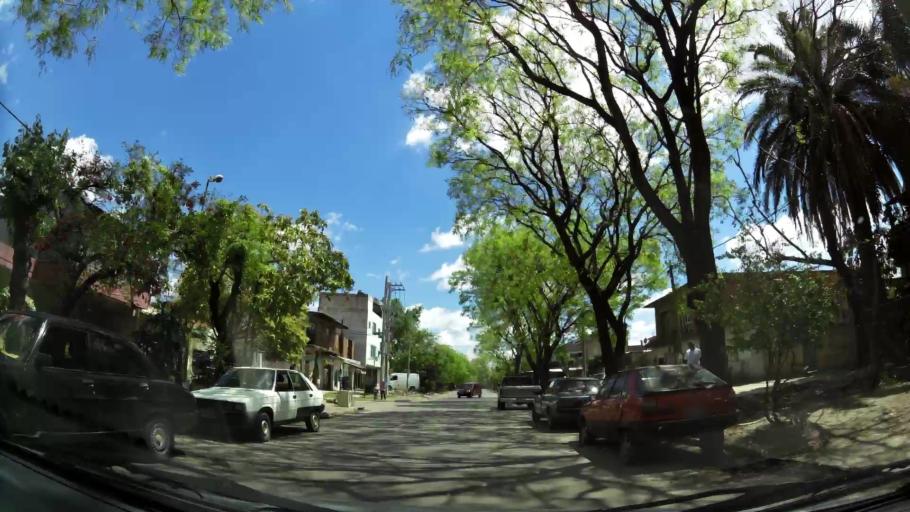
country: AR
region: Buenos Aires
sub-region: Partido de Lanus
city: Lanus
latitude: -34.6965
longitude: -58.4317
